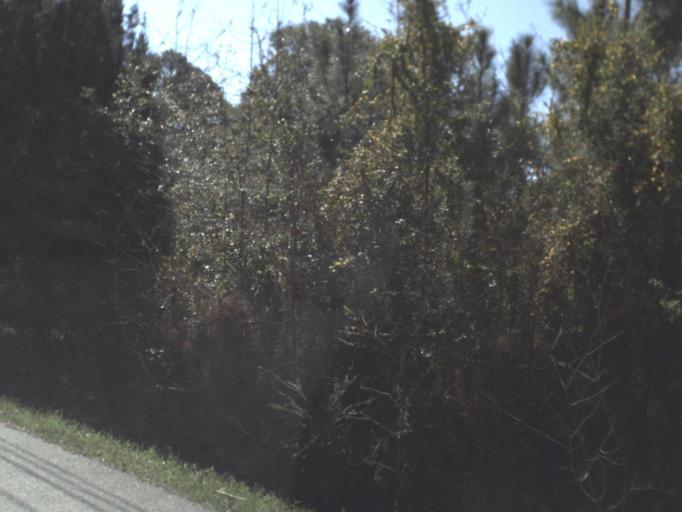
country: US
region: Florida
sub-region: Bay County
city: Pretty Bayou
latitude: 30.1943
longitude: -85.6870
